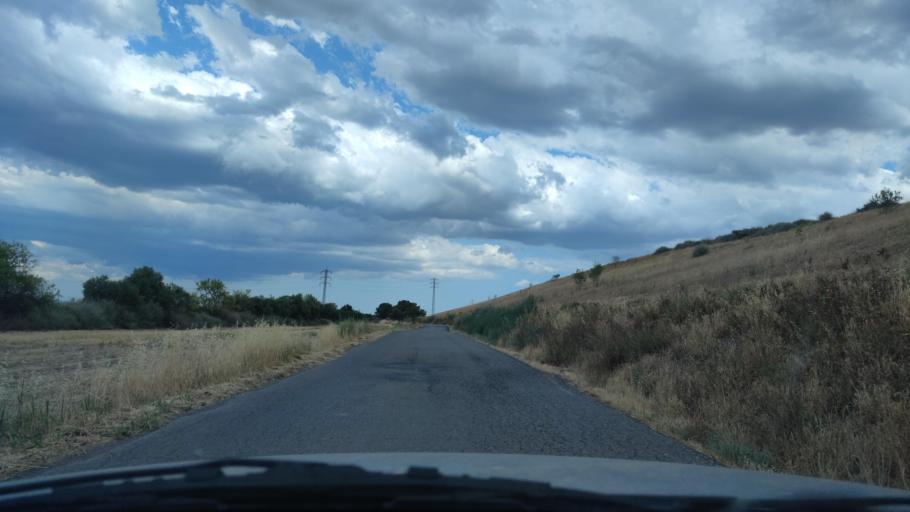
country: ES
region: Catalonia
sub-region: Provincia de Lleida
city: Lleida
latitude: 41.6174
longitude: 0.5745
